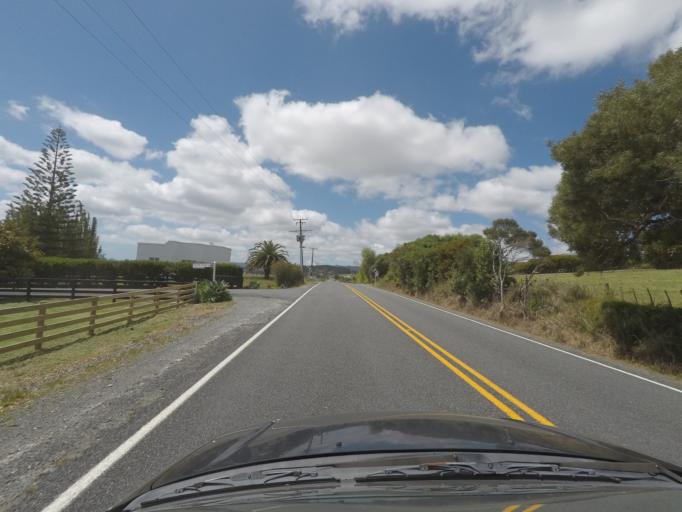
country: NZ
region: Northland
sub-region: Whangarei
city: Ruakaka
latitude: -36.0042
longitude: 174.4776
